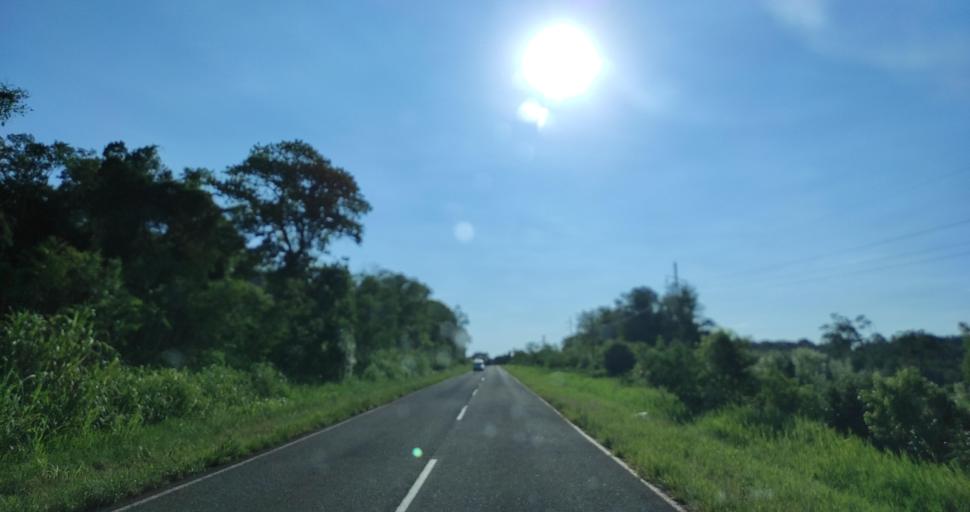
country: AR
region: Misiones
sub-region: Departamento de Eldorado
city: Eldorado
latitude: -26.3762
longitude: -54.3320
